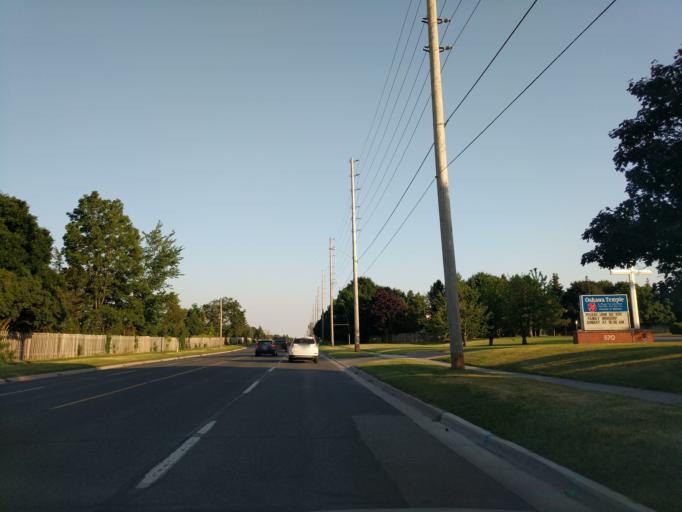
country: CA
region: Ontario
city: Oshawa
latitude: 43.9070
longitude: -78.9002
